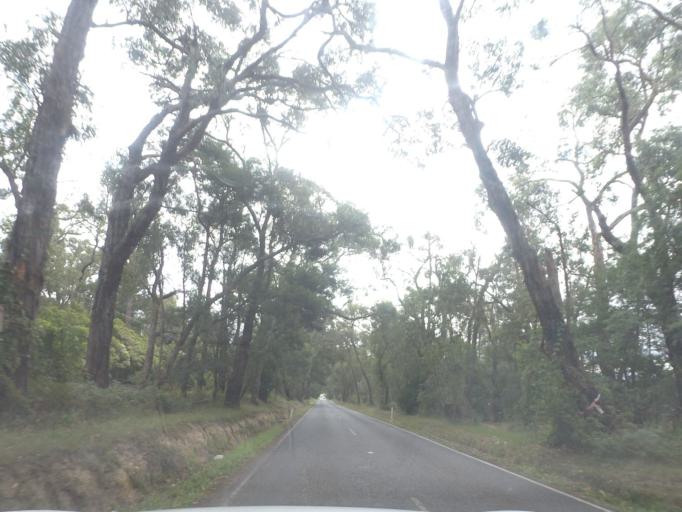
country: AU
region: Victoria
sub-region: Maroondah
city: Kilsyth South
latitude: -37.8296
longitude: 145.3246
